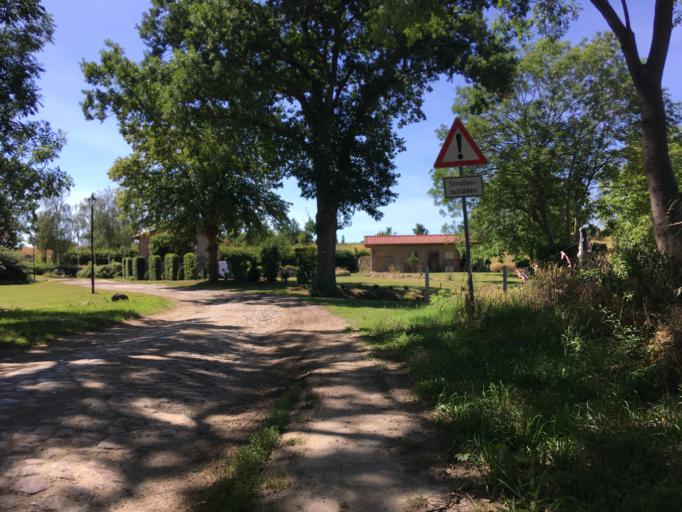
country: DE
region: Brandenburg
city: Brussow
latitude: 53.3224
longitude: 14.1156
